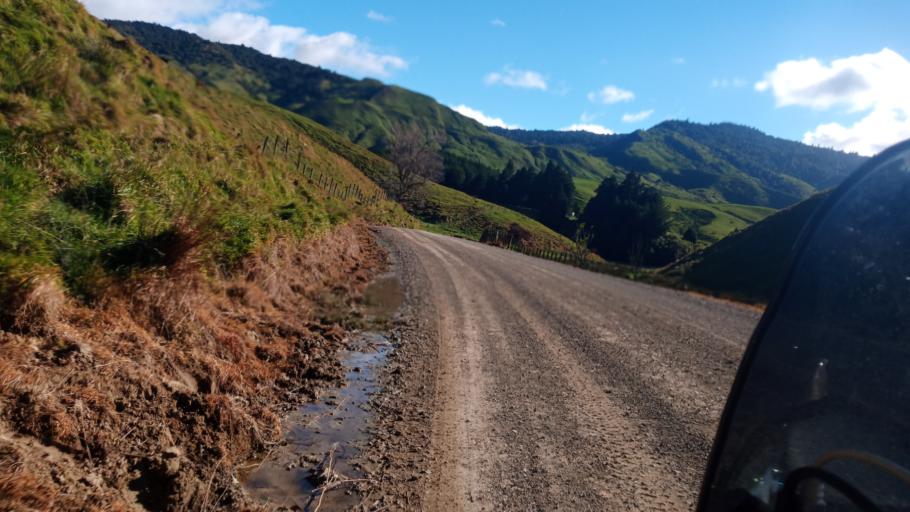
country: NZ
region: Hawke's Bay
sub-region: Wairoa District
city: Wairoa
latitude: -38.7687
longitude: 177.2635
